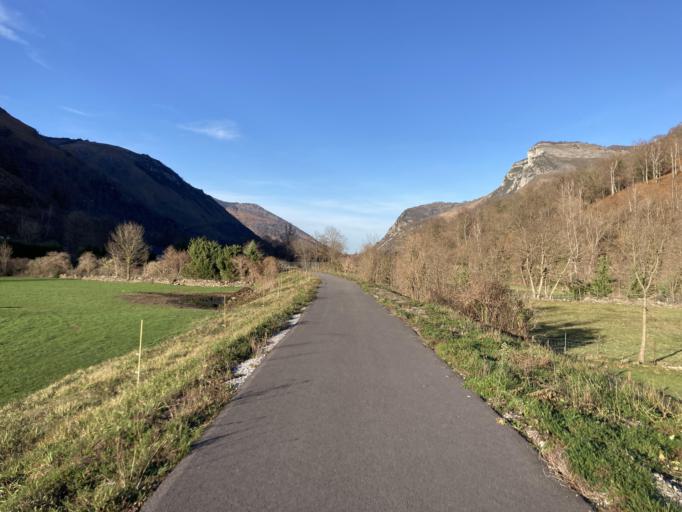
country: FR
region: Aquitaine
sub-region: Departement des Pyrenees-Atlantiques
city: Laruns
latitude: 43.0051
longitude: -0.4192
